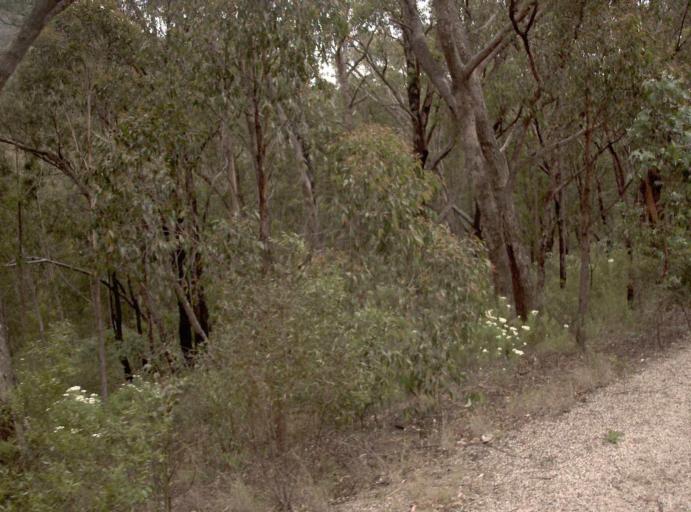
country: AU
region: Victoria
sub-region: East Gippsland
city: Bairnsdale
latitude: -37.6052
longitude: 147.1894
